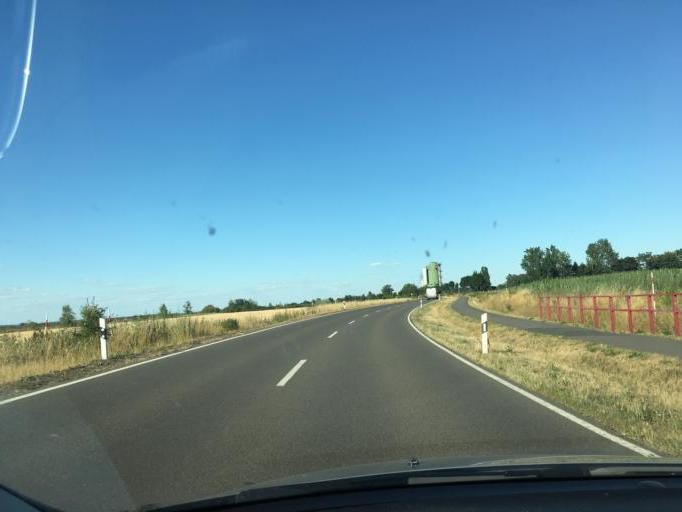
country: DE
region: Saxony
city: Grossposna
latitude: 51.2633
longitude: 12.4795
